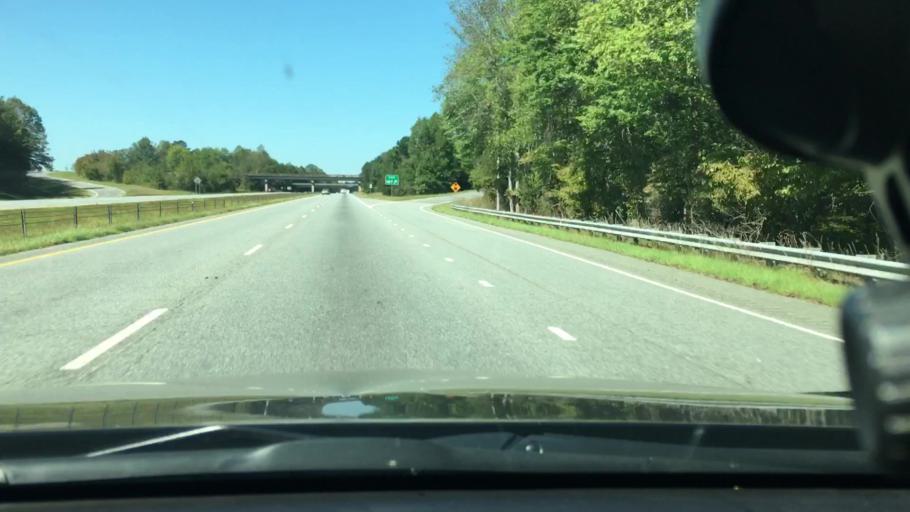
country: US
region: North Carolina
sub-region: Rutherford County
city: Forest City
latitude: 35.3036
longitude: -81.7707
